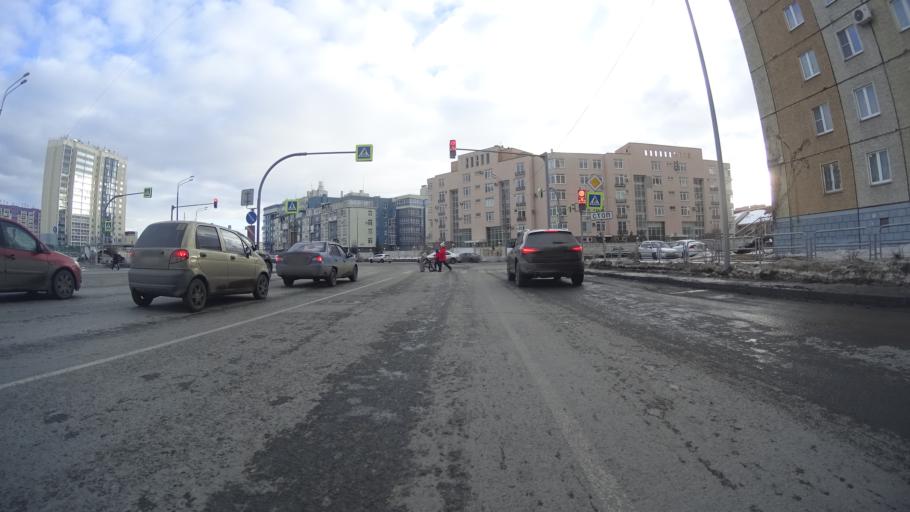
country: RU
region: Chelyabinsk
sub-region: Gorod Chelyabinsk
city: Chelyabinsk
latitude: 55.1606
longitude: 61.3022
